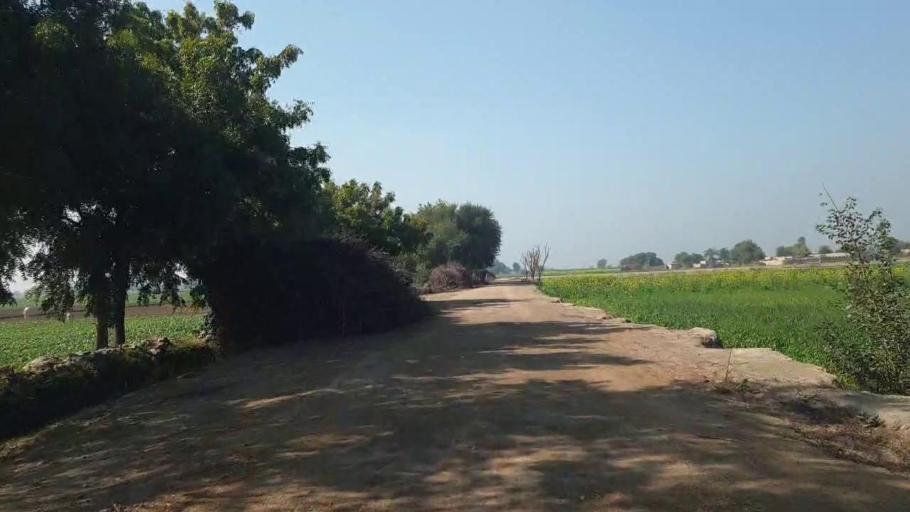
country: PK
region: Sindh
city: Shahdadpur
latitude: 25.9491
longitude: 68.5391
